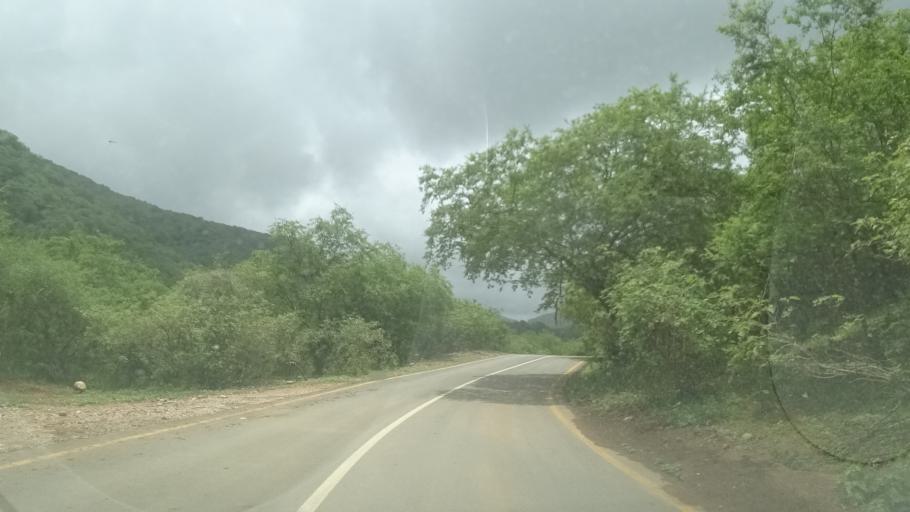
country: OM
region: Zufar
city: Salalah
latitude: 17.1042
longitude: 54.3504
